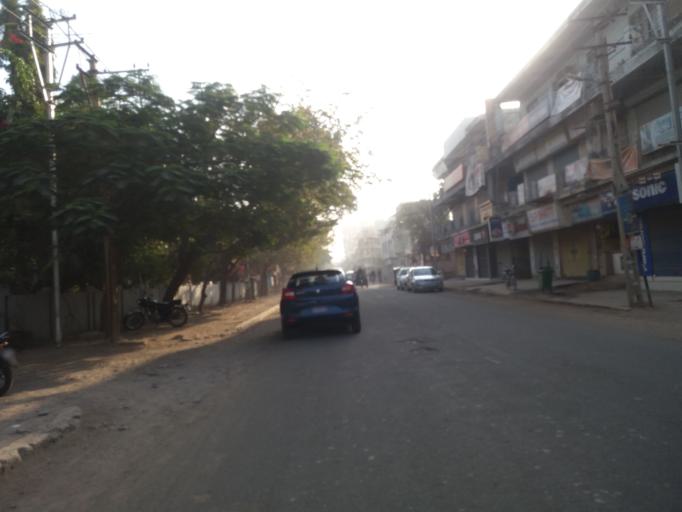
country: IN
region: Gujarat
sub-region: Porbandar
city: Porbandar
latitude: 21.6388
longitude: 69.6170
